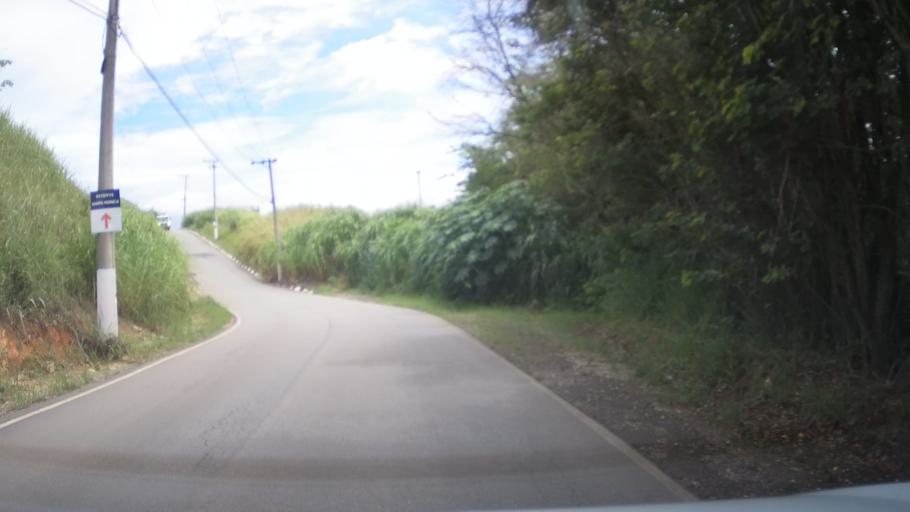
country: BR
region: Sao Paulo
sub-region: Louveira
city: Louveira
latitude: -23.0924
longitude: -47.0165
